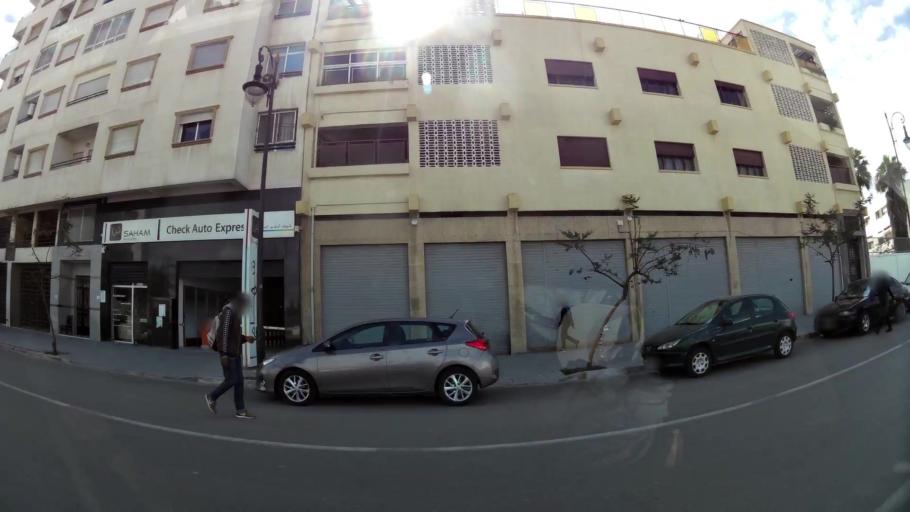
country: MA
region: Tanger-Tetouan
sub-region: Tanger-Assilah
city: Tangier
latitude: 35.7663
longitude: -5.8141
